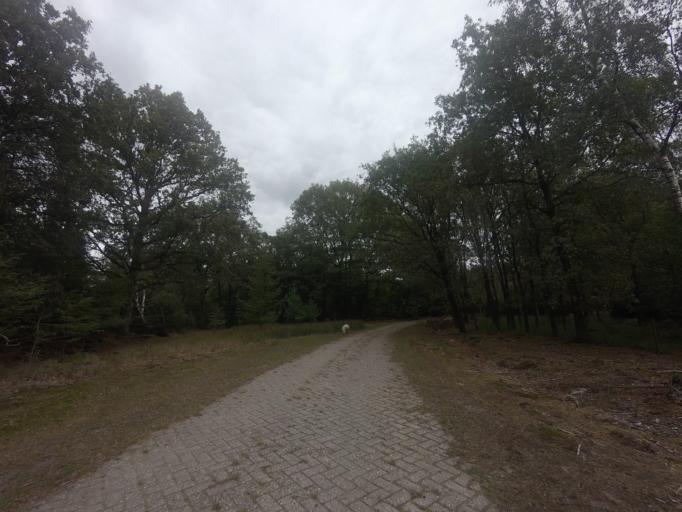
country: NL
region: Drenthe
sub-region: Gemeente Westerveld
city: Dwingeloo
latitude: 52.9154
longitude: 6.3067
